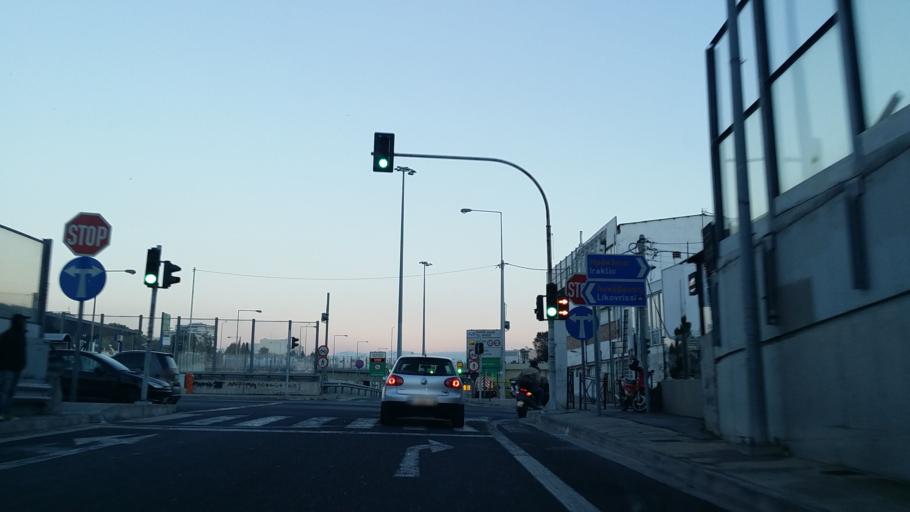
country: GR
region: Attica
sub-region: Nomarchia Athinas
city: Irakleio
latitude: 38.0572
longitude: 23.7709
